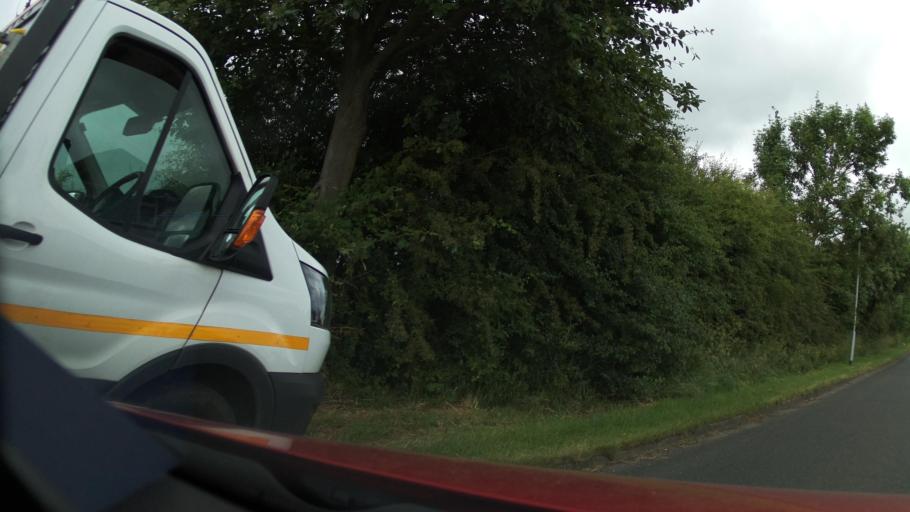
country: GB
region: England
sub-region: Leicestershire
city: Coalville
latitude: 52.7337
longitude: -1.3500
